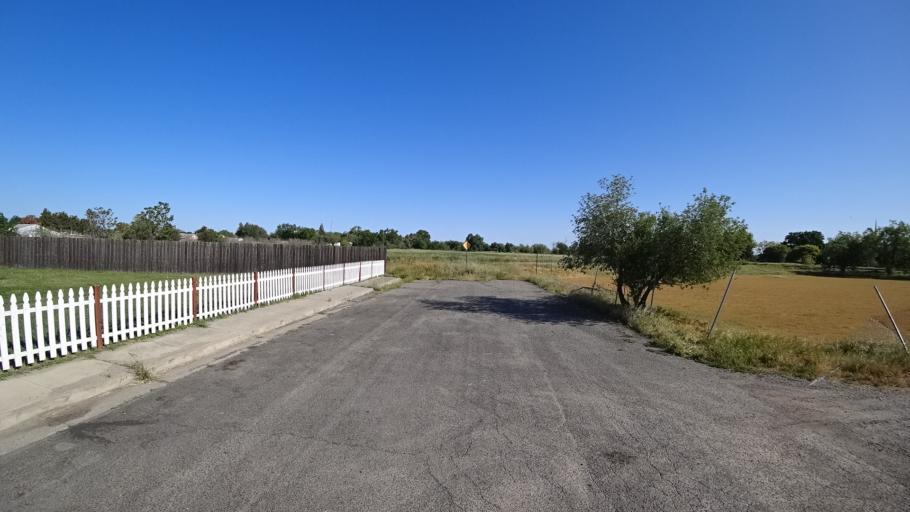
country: US
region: California
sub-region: Glenn County
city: Orland
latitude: 39.7532
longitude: -122.1866
